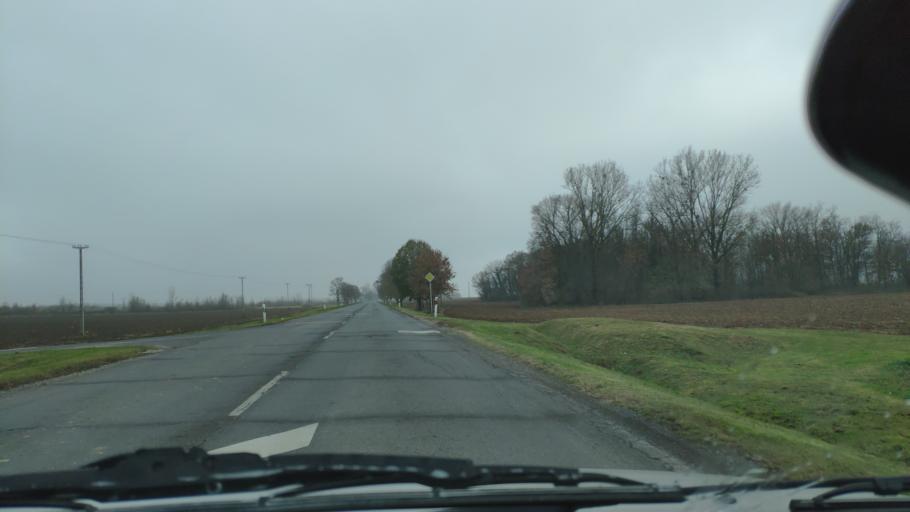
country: HU
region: Zala
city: Zalakomar
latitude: 46.5859
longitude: 17.2634
